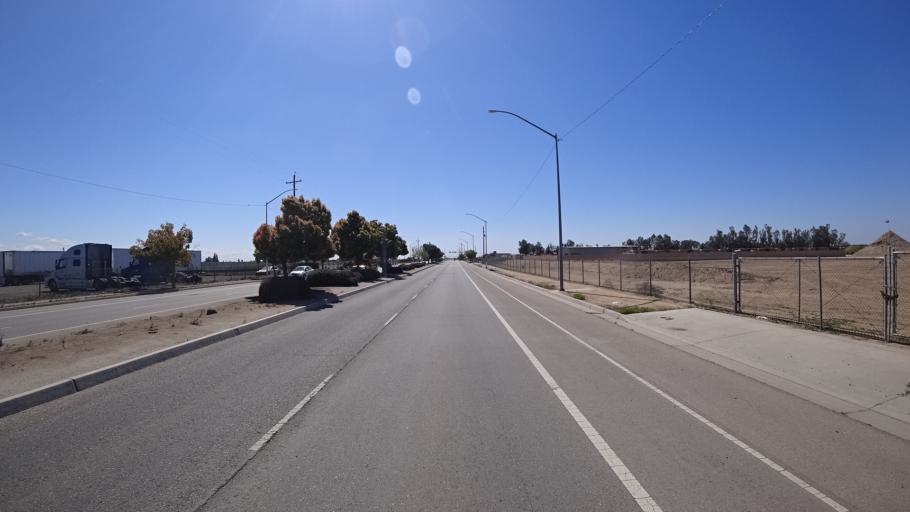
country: US
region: California
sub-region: Fresno County
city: West Park
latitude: 36.7488
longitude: -119.8444
